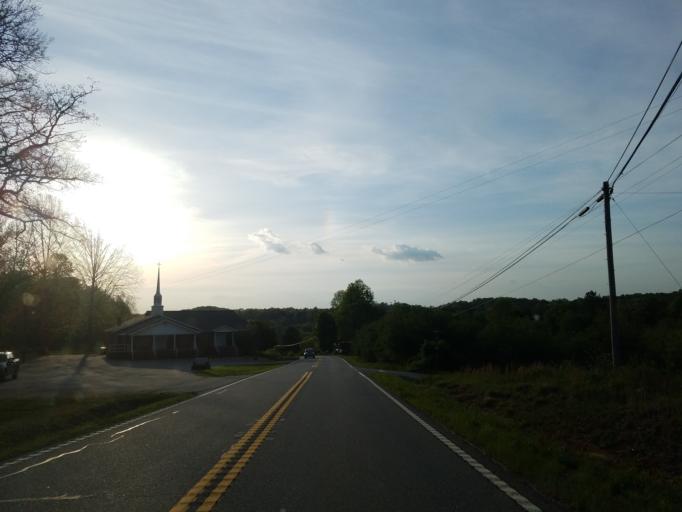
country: US
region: Georgia
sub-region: Fannin County
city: Blue Ridge
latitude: 34.8444
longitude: -84.2097
